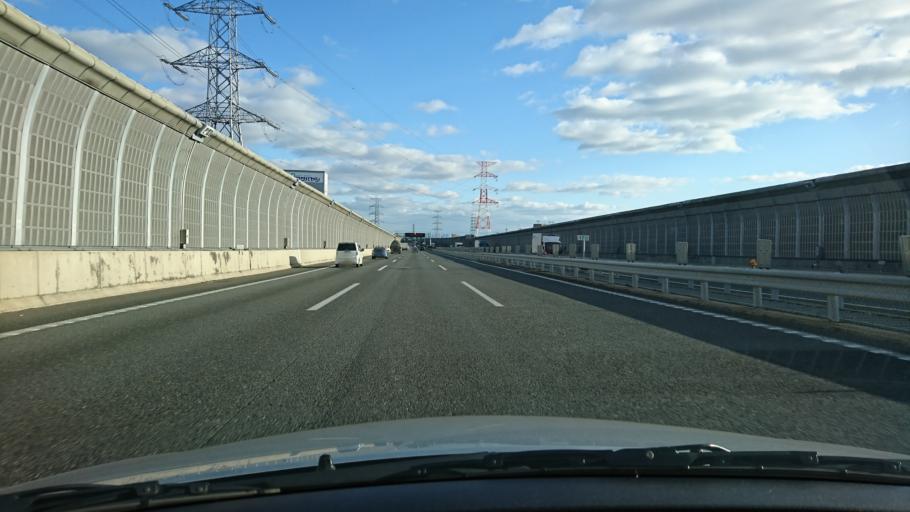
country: JP
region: Hyogo
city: Takarazuka
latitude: 34.8118
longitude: 135.3618
